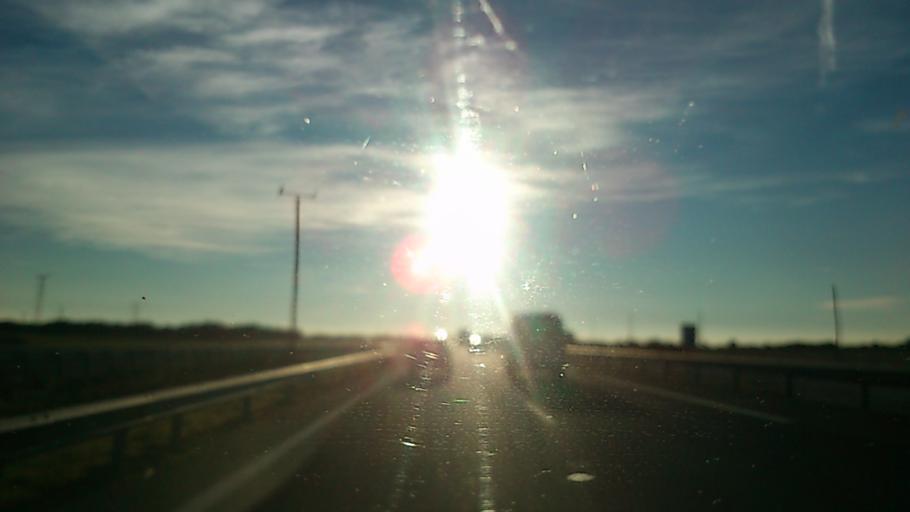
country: ES
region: Castille-La Mancha
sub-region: Provincia de Guadalajara
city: Utande
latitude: 40.8240
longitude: -2.9195
